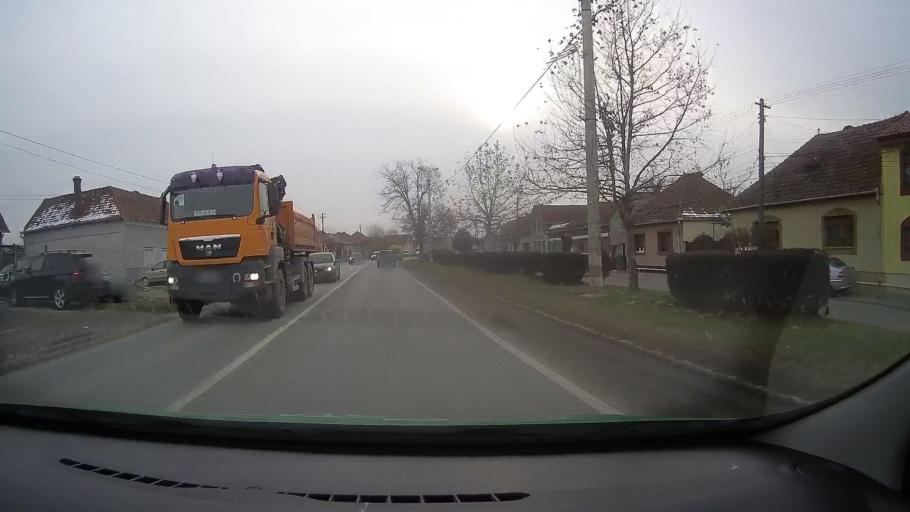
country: RO
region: Hunedoara
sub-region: Municipiul Orastie
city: Orastie
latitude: 45.8485
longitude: 23.2065
